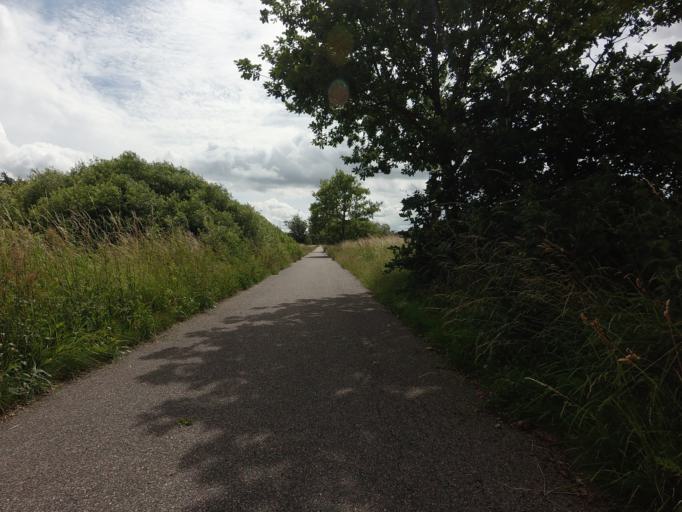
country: DK
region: Central Jutland
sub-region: Randers Kommune
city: Langa
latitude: 56.3739
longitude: 9.8979
